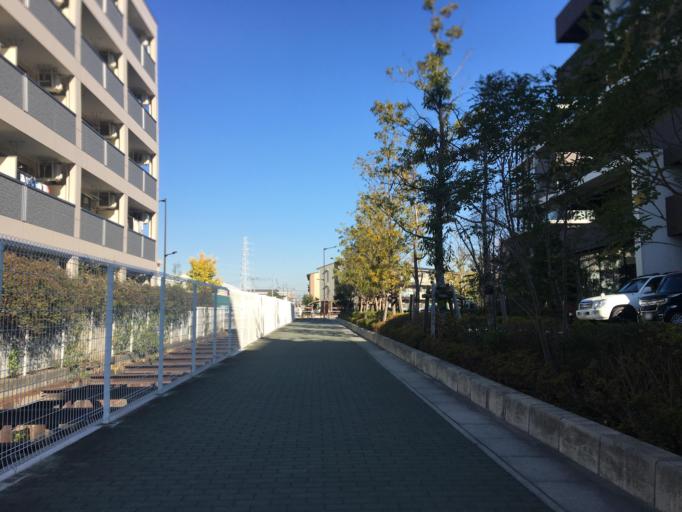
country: JP
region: Saitama
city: Yashio-shi
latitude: 35.8077
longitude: 139.8498
